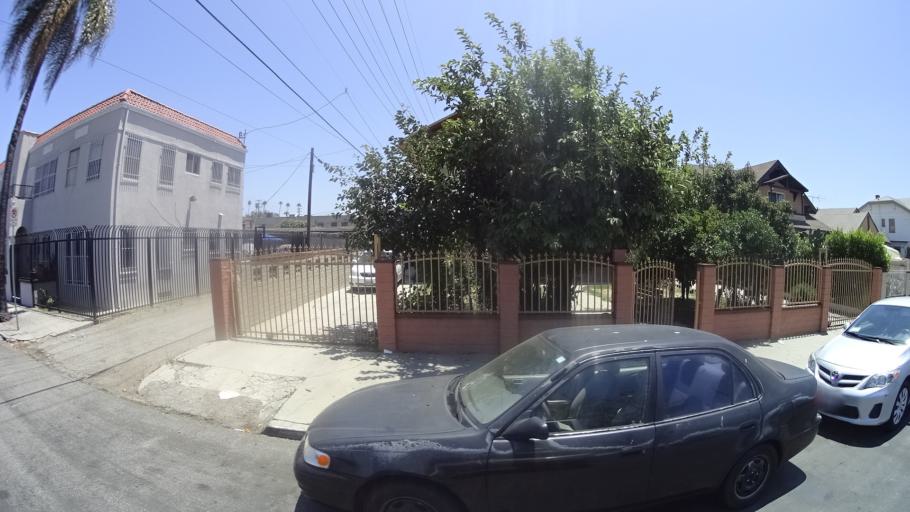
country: US
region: California
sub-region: Los Angeles County
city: View Park-Windsor Hills
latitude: 33.9990
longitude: -118.3098
